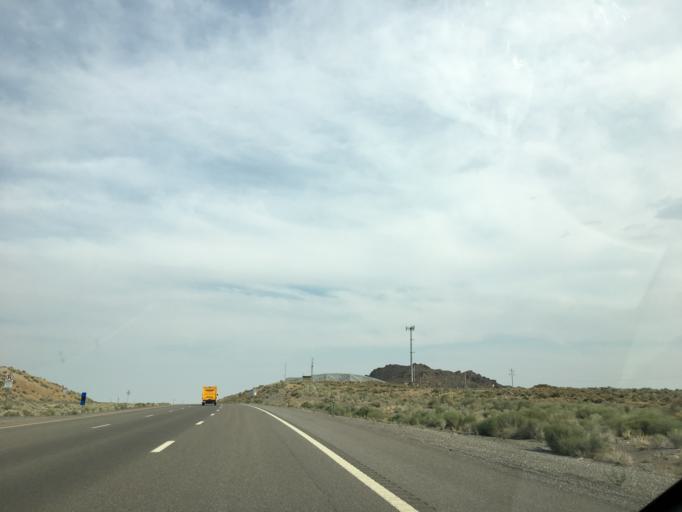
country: US
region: Nevada
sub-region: Elko County
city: West Wendover
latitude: 40.7480
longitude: -114.1082
